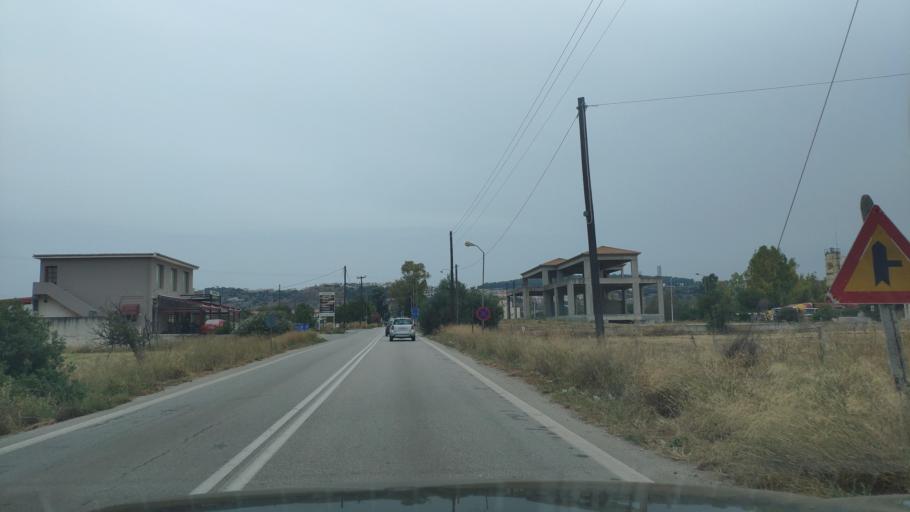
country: GR
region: Peloponnese
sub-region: Nomos Argolidos
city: Kranidi
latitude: 37.3968
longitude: 23.1564
